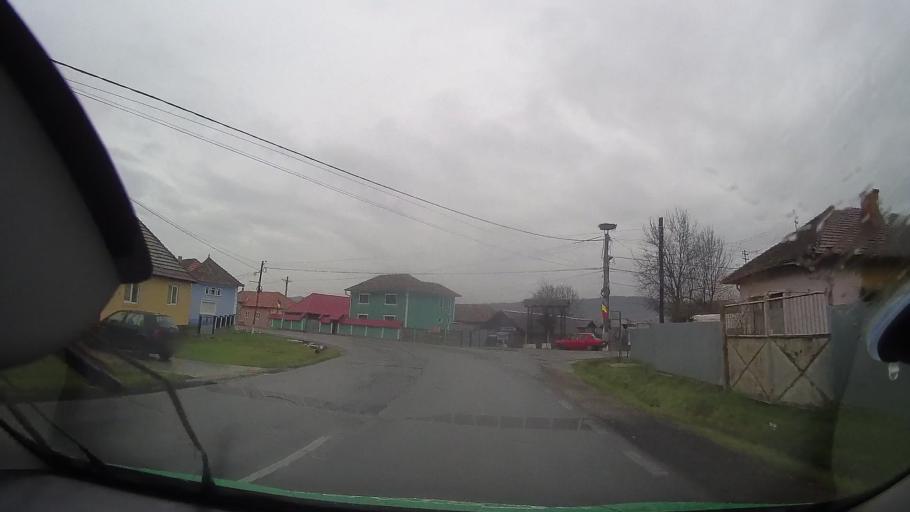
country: RO
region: Bihor
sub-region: Comuna Rabagani
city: Rabagani
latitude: 46.7477
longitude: 22.2263
